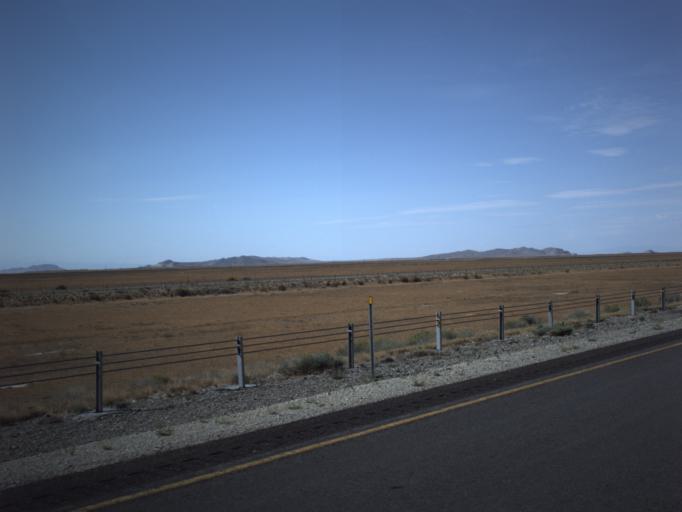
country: US
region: Utah
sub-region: Tooele County
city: Grantsville
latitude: 40.7260
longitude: -113.1490
